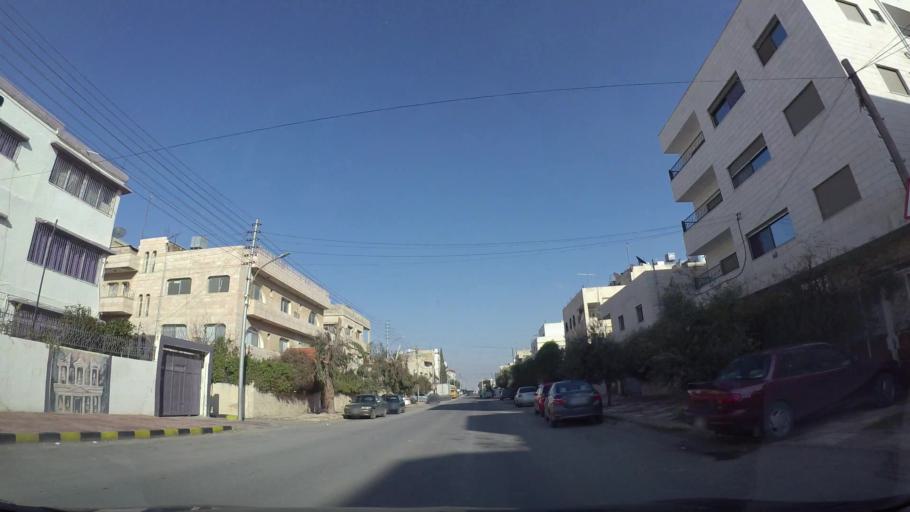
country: JO
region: Amman
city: Amman
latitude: 31.9800
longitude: 35.9575
